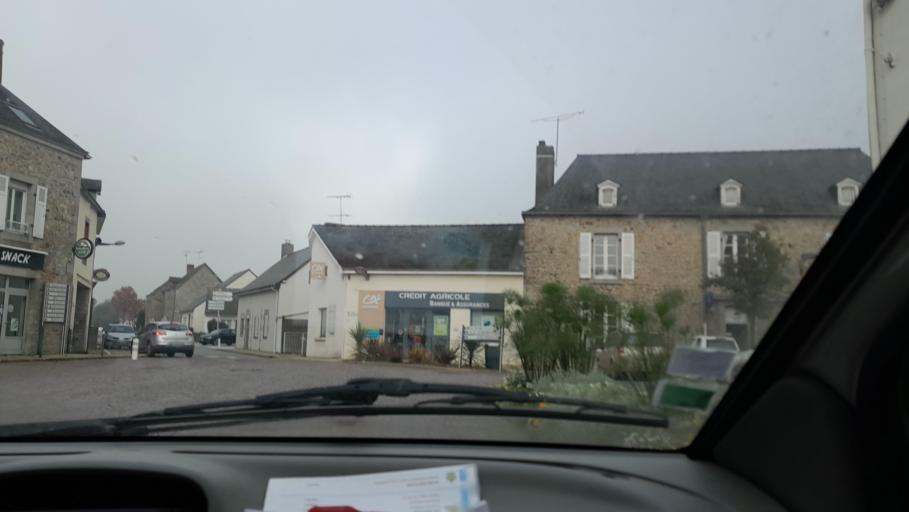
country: FR
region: Pays de la Loire
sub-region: Departement de la Mayenne
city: Saint-Pierre-la-Cour
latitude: 48.1149
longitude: -1.0267
